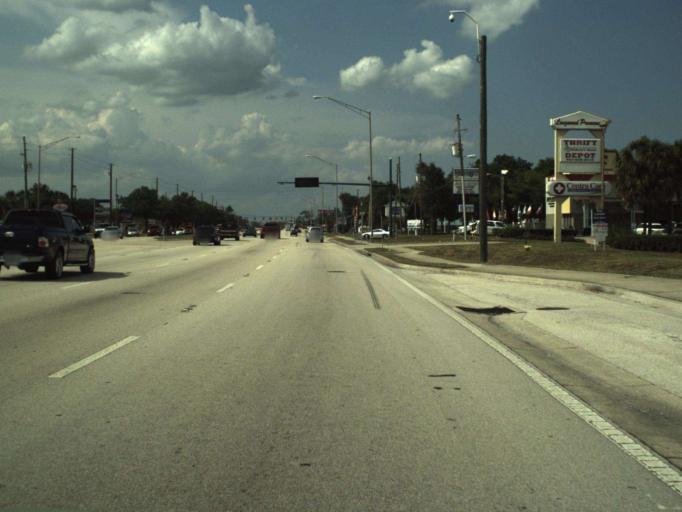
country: US
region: Florida
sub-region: Seminole County
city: Casselberry
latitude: 28.6928
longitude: -81.3275
